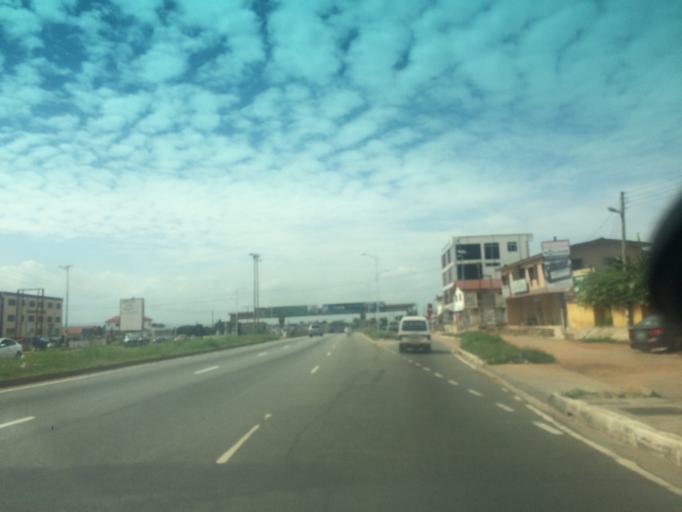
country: GH
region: Greater Accra
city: Medina Estates
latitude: 5.6698
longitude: -0.1759
